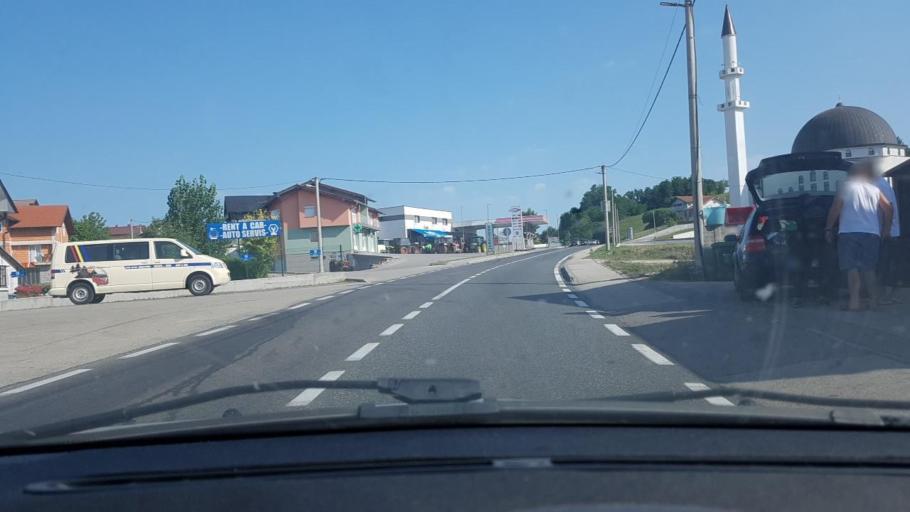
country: BA
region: Federation of Bosnia and Herzegovina
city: Ostrozac
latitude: 44.9097
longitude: 15.9314
